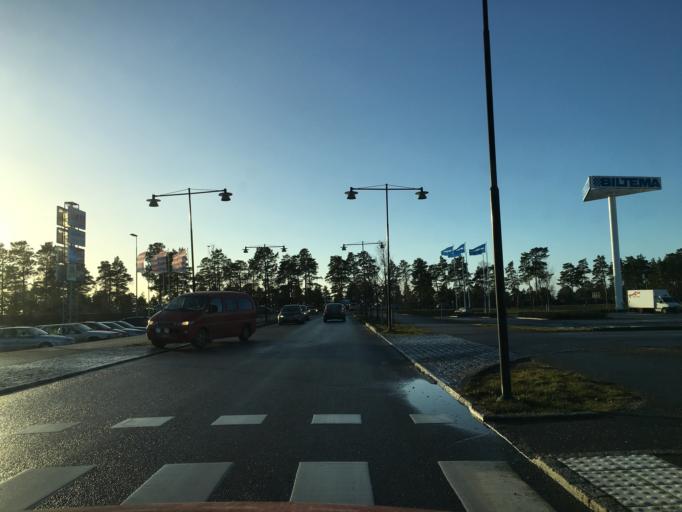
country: SE
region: Kalmar
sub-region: Vasterviks Kommun
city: Vaestervik
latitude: 57.7682
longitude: 16.5951
